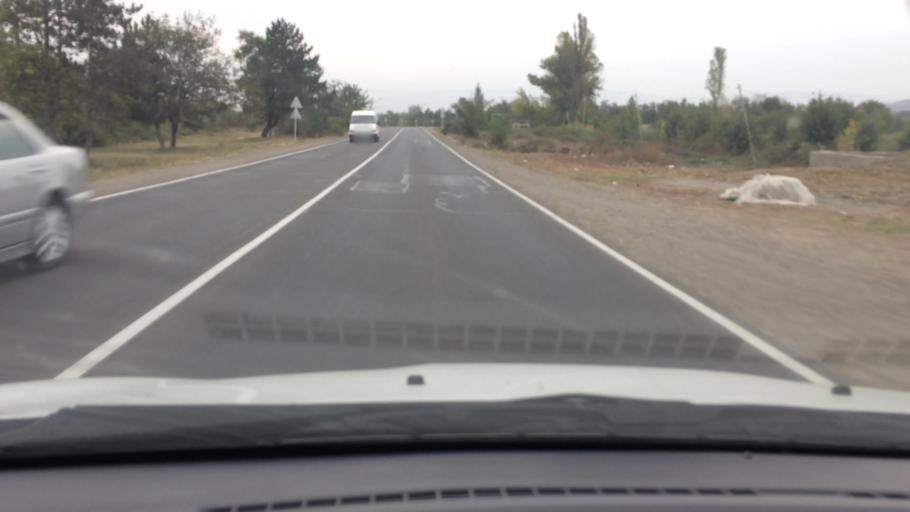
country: GE
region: Kvemo Kartli
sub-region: Marneuli
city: Marneuli
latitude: 41.4119
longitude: 44.8299
